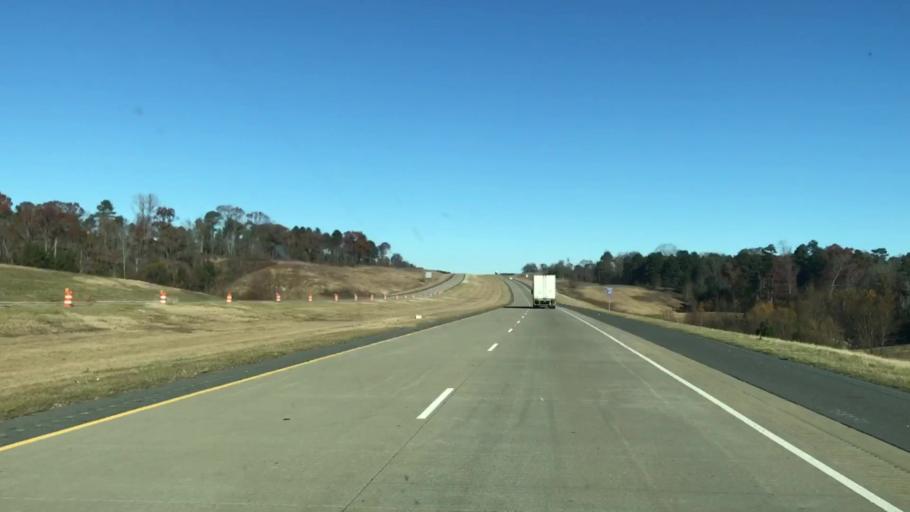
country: US
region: Louisiana
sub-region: Caddo Parish
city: Vivian
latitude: 32.9502
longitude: -93.8991
